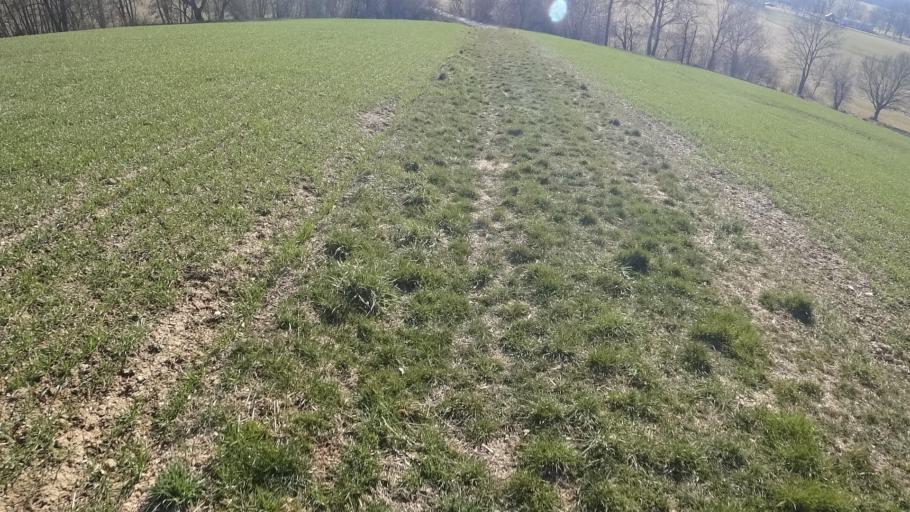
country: DE
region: Rheinland-Pfalz
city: Mutterschied
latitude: 49.9853
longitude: 7.5641
